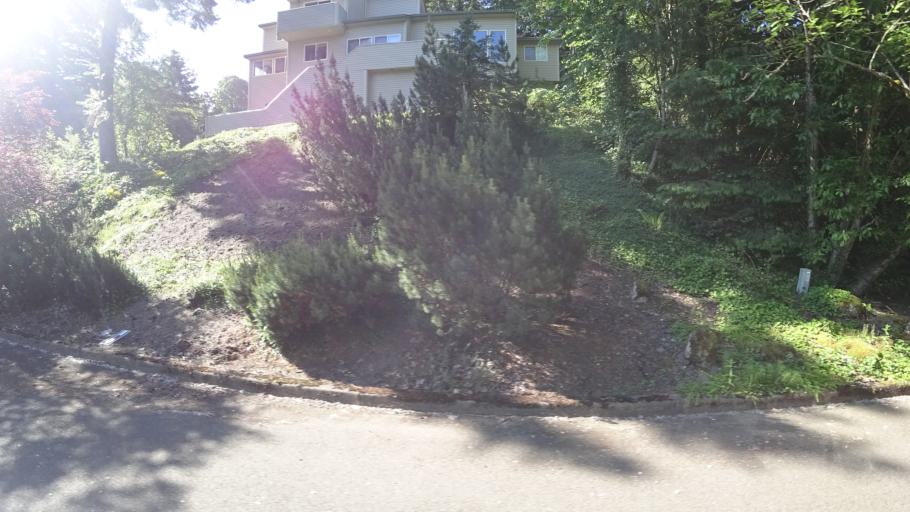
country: US
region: Oregon
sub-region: Clackamas County
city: Happy Valley
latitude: 45.4679
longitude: -122.5406
